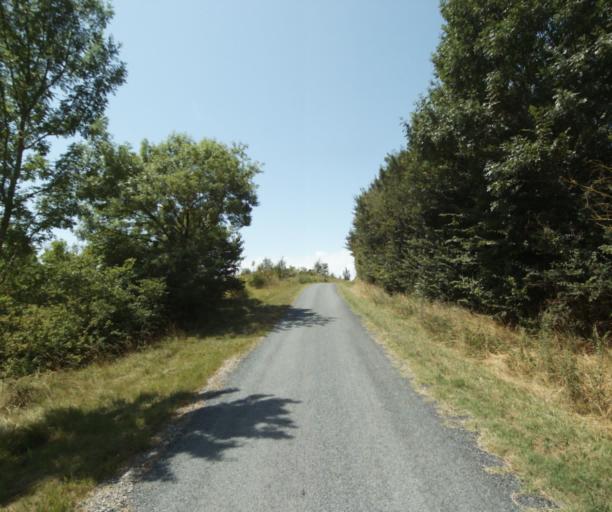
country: FR
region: Midi-Pyrenees
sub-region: Departement de la Haute-Garonne
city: Auriac-sur-Vendinelle
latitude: 43.4605
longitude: 1.8243
